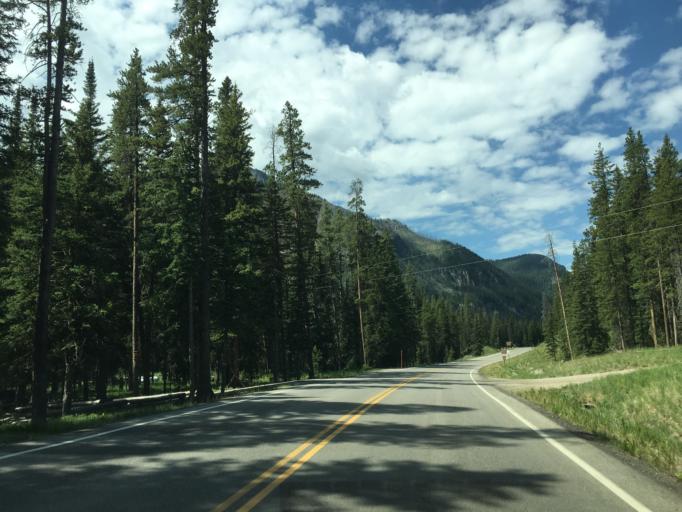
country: US
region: Montana
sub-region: Stillwater County
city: Absarokee
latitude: 45.0055
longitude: -109.9926
